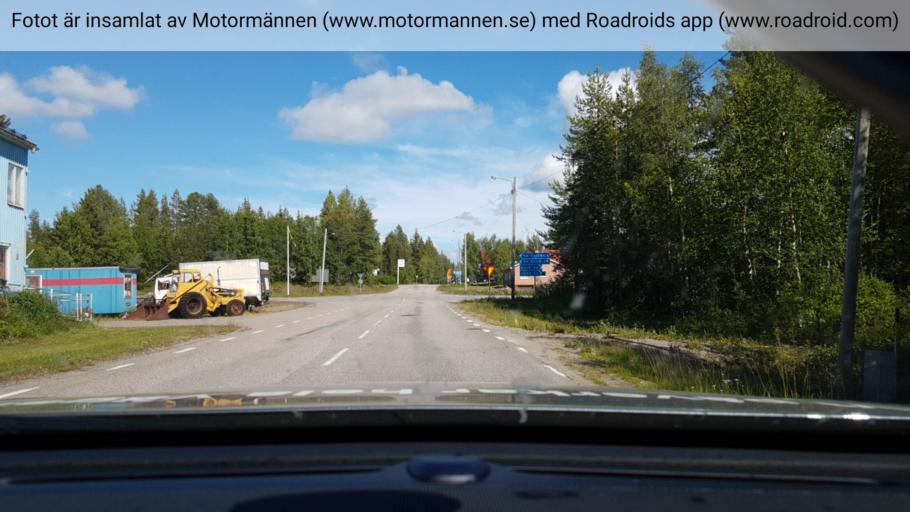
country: SE
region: Norrbotten
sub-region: Arjeplogs Kommun
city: Arjeplog
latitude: 65.5856
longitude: 18.1621
